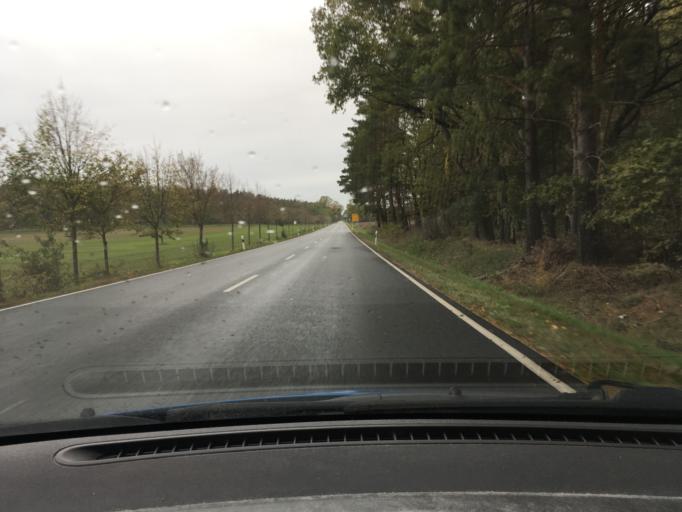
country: DE
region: Saxony-Anhalt
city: Klieken
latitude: 51.8938
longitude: 12.3594
